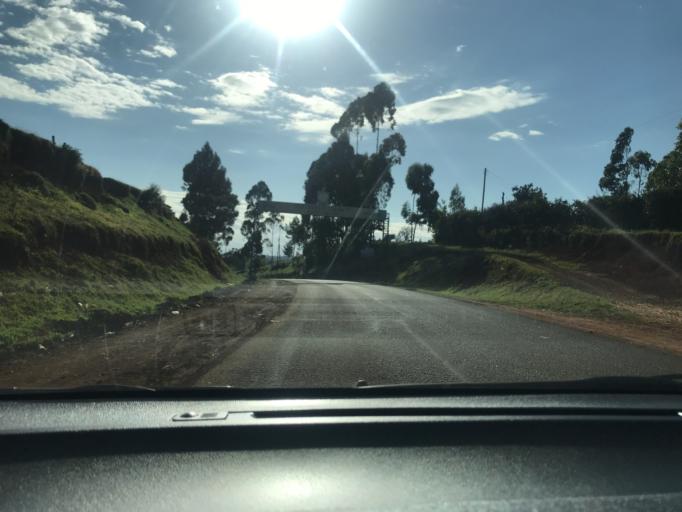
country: KE
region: Kirinyaga
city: Keruguya
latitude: -0.4795
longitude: 37.1747
